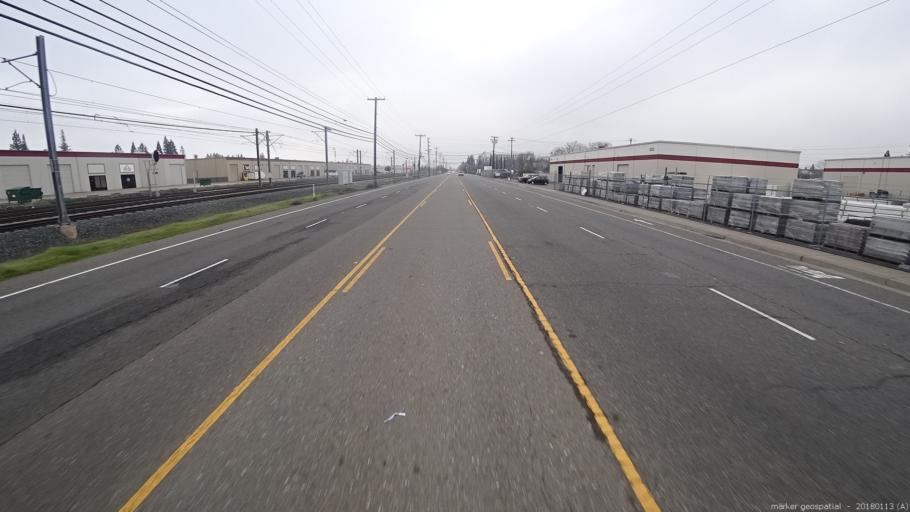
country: US
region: California
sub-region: Sacramento County
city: Gold River
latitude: 38.6091
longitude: -121.2624
